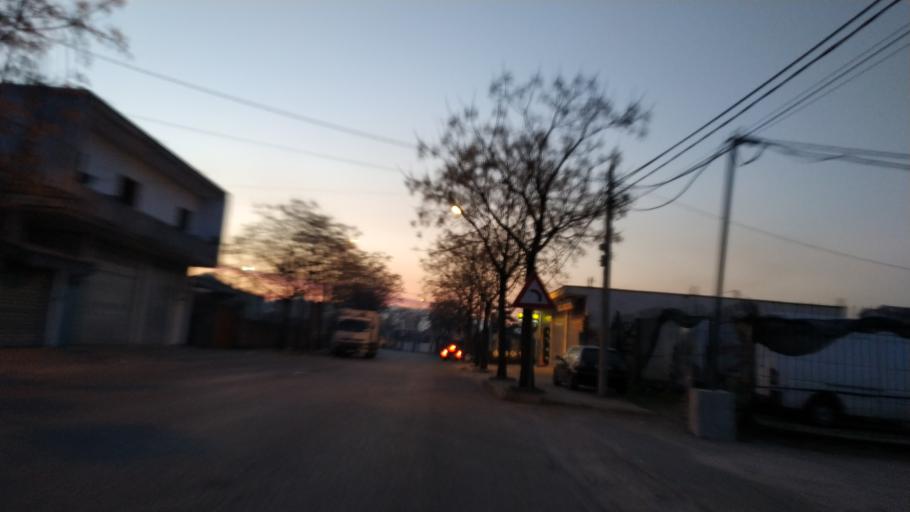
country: AL
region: Shkoder
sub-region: Rrethi i Shkodres
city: Shkoder
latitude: 42.0780
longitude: 19.5076
